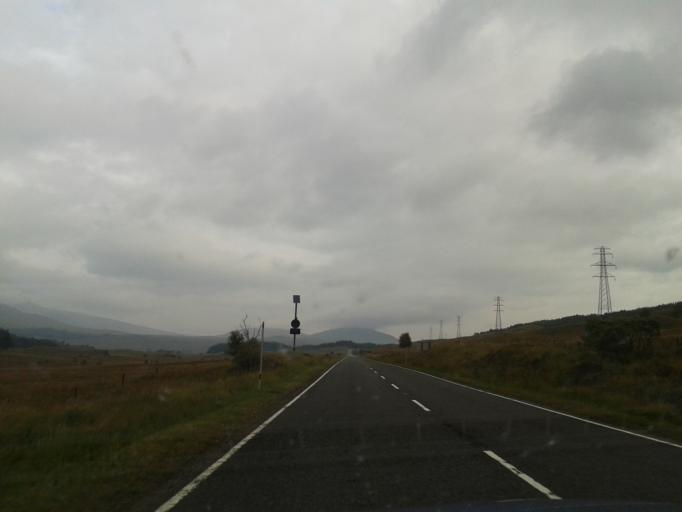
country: GB
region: Scotland
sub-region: Highland
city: Spean Bridge
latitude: 56.5226
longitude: -4.7671
